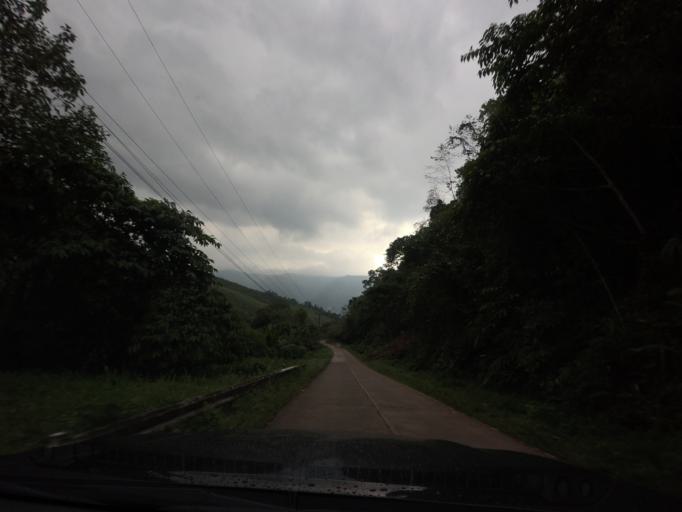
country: TH
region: Nan
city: Bo Kluea
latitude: 19.1952
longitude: 101.1915
